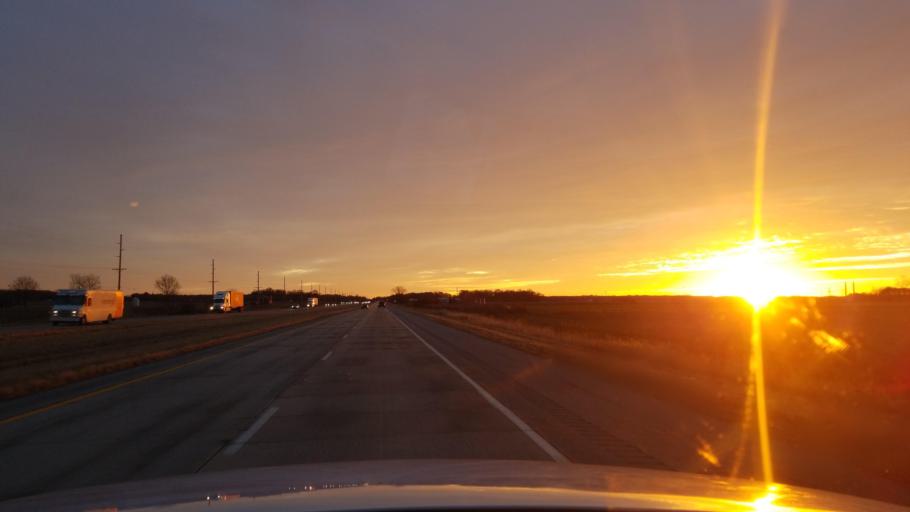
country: US
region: Indiana
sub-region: Posey County
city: Mount Vernon
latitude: 37.9420
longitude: -87.7800
